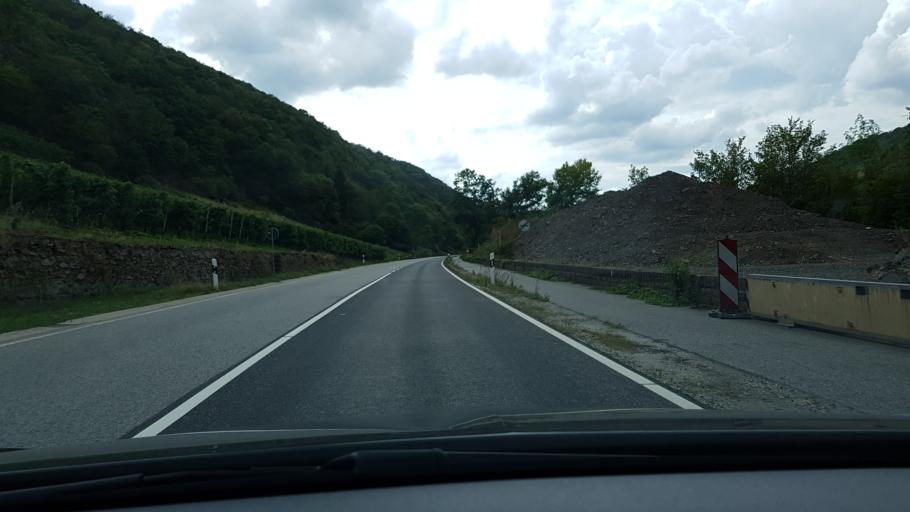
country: DE
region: Rheinland-Pfalz
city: Niederfell
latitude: 50.2732
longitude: 7.4602
